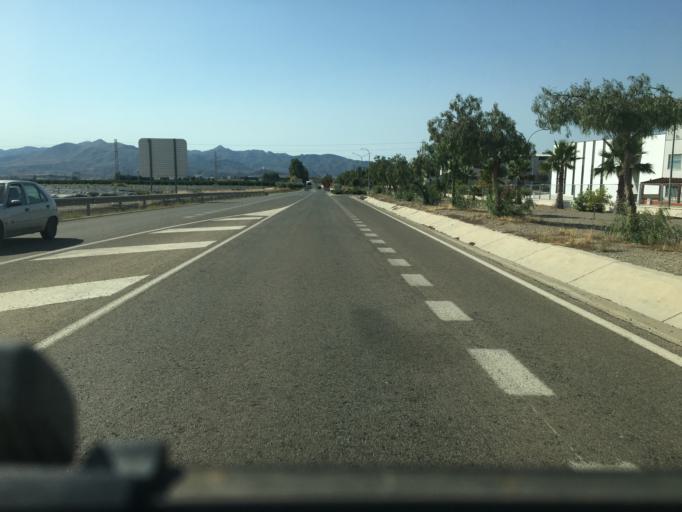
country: ES
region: Andalusia
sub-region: Provincia de Almeria
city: Huercal-Overa
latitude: 37.4168
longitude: -1.9669
